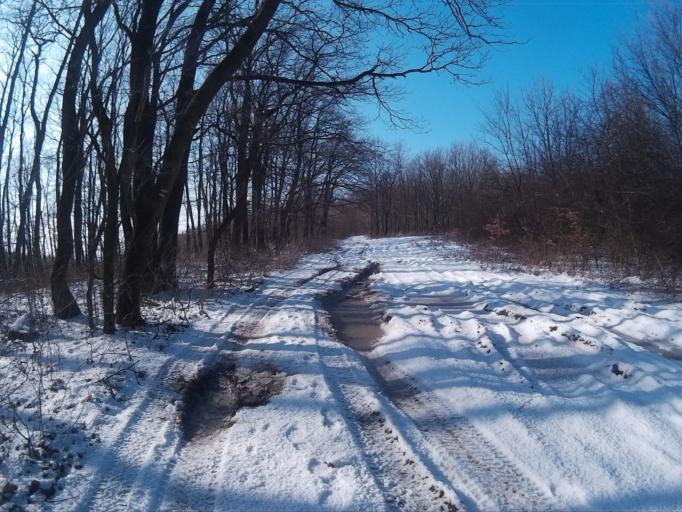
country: HU
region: Komarom-Esztergom
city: Labatlan
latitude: 47.7105
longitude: 18.4968
